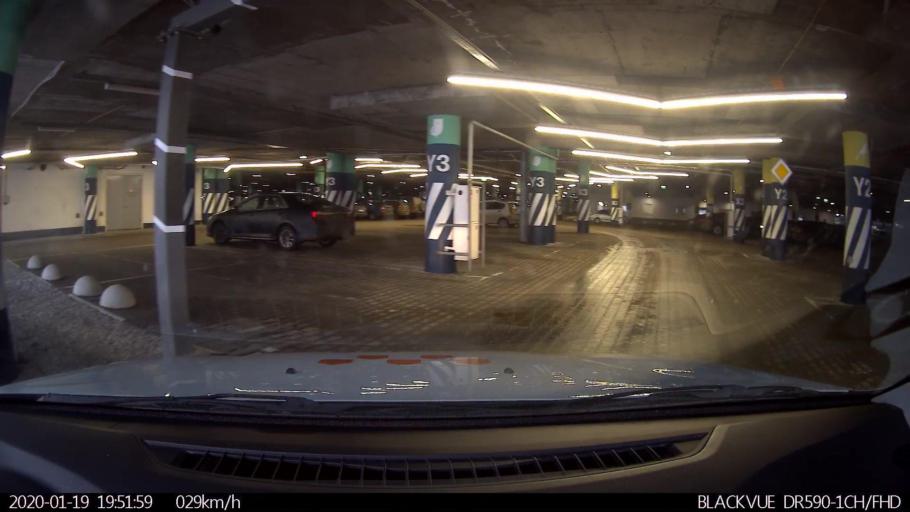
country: RU
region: Nizjnij Novgorod
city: Afonino
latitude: 56.2242
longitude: 44.0688
